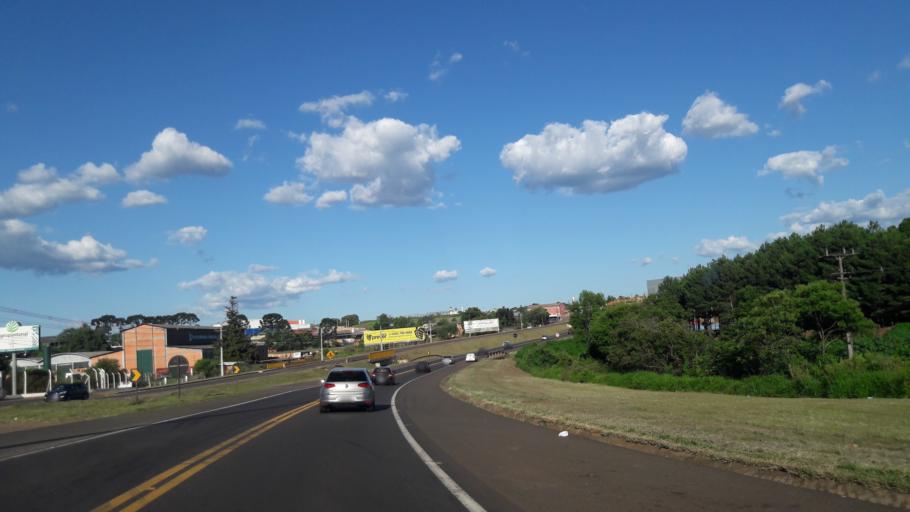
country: BR
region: Parana
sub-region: Guarapuava
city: Guarapuava
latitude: -25.3665
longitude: -51.4922
